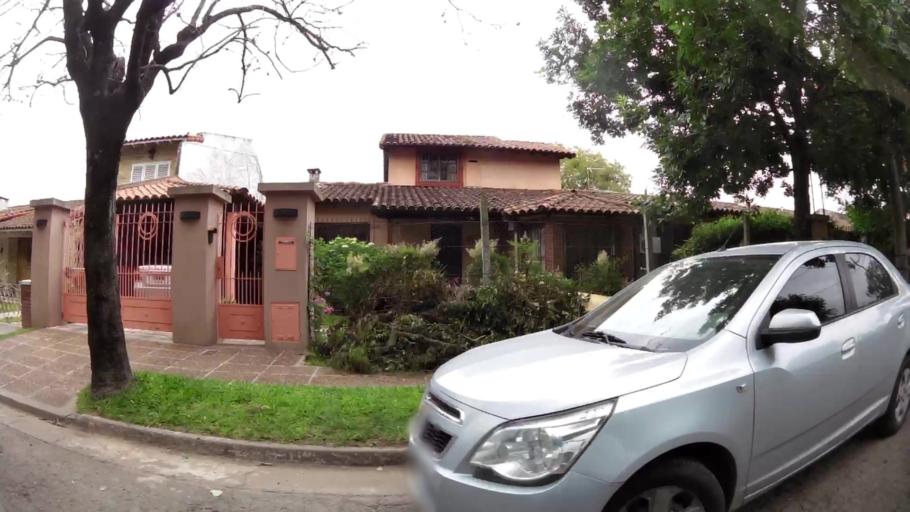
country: AR
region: Buenos Aires
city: San Justo
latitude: -34.7320
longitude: -58.5277
